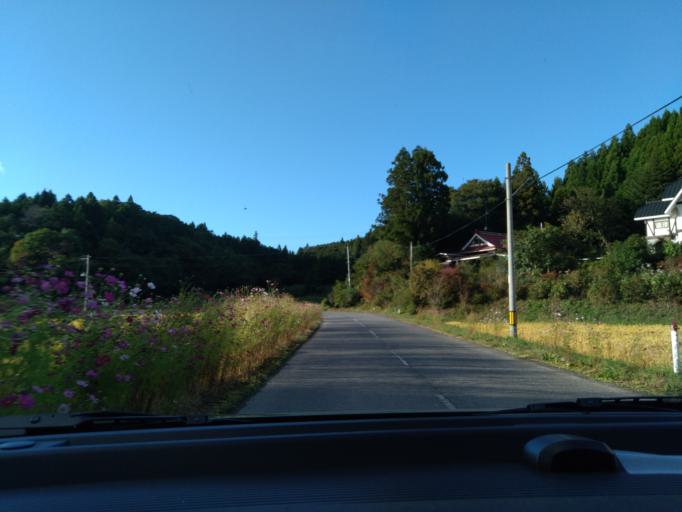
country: JP
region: Iwate
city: Ichinoseki
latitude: 38.8698
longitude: 141.1750
